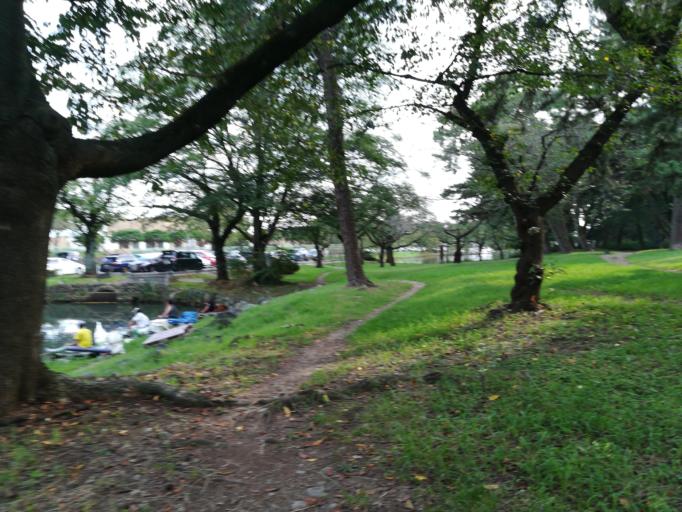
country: JP
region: Gunma
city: Maebashi-shi
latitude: 36.4178
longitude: 139.0526
